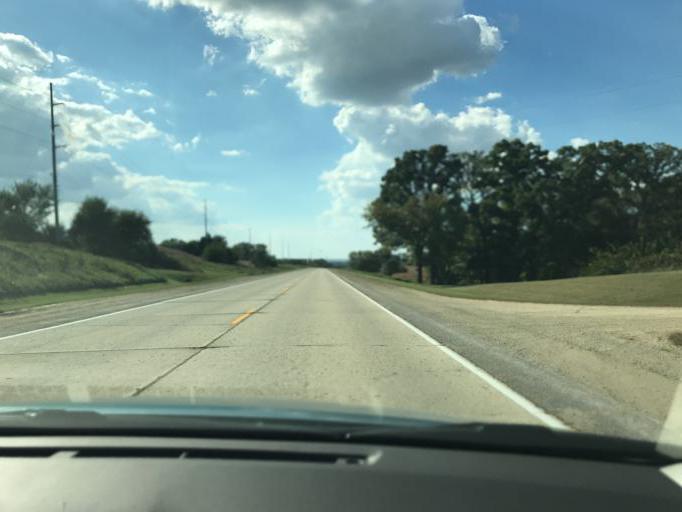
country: US
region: Wisconsin
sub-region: Green County
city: Brodhead
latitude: 42.5597
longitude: -89.3155
